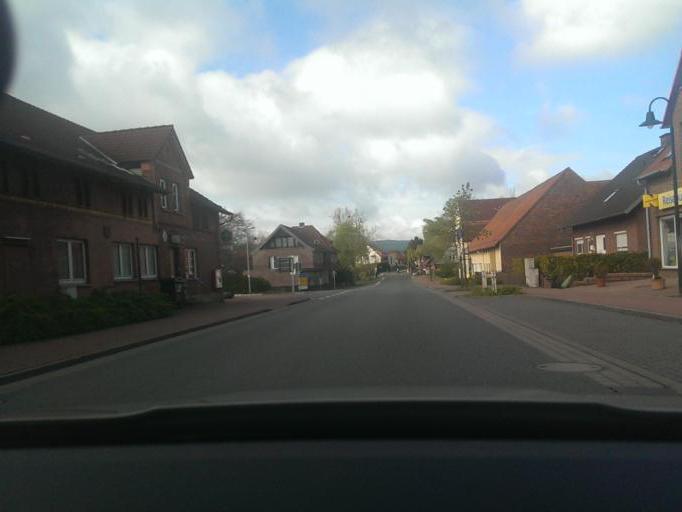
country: DE
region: Lower Saxony
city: Rehren
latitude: 52.2328
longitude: 9.2363
